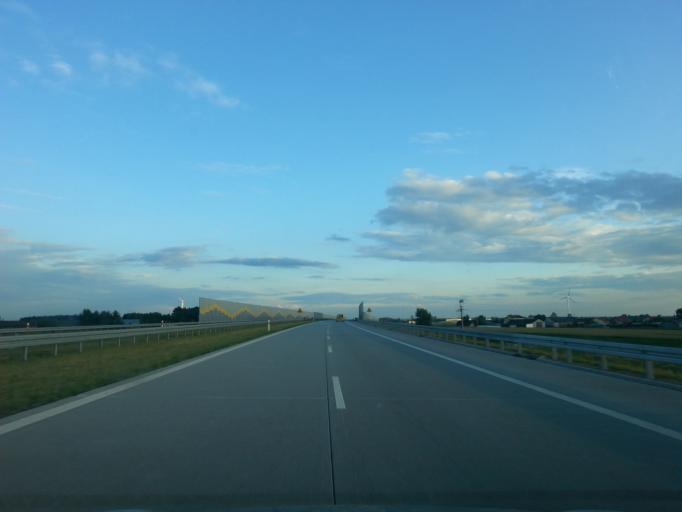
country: PL
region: Lodz Voivodeship
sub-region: Powiat sieradzki
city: Zloczew
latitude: 51.4239
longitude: 18.6451
